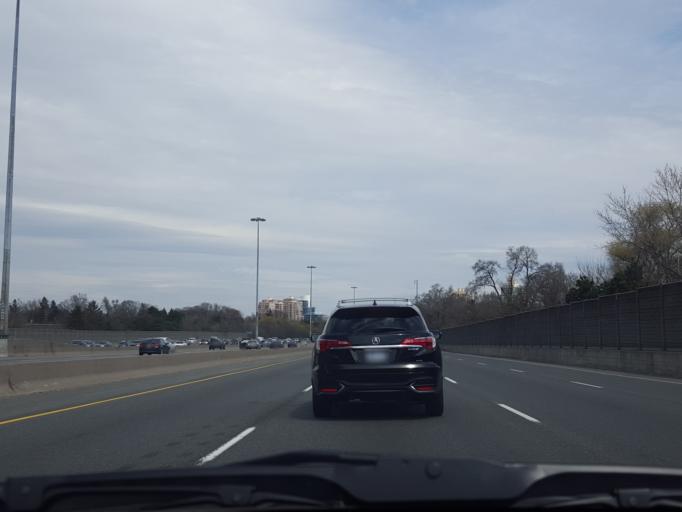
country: CA
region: Ontario
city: Willowdale
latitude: 43.7571
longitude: -79.4021
